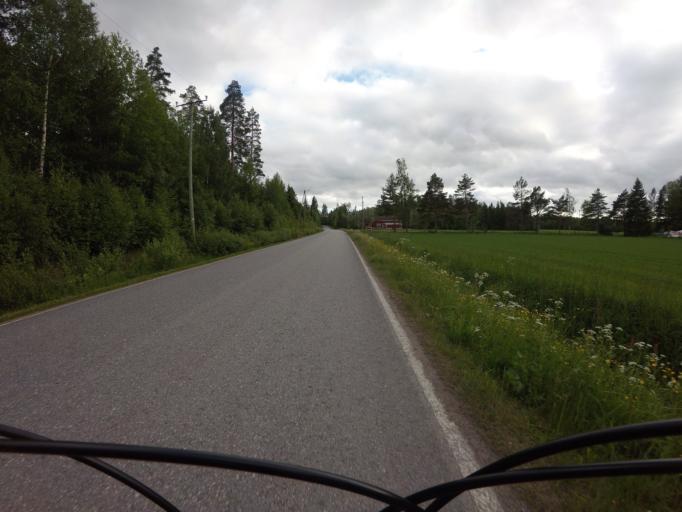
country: FI
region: Varsinais-Suomi
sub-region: Turku
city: Lieto
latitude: 60.5273
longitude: 22.3855
